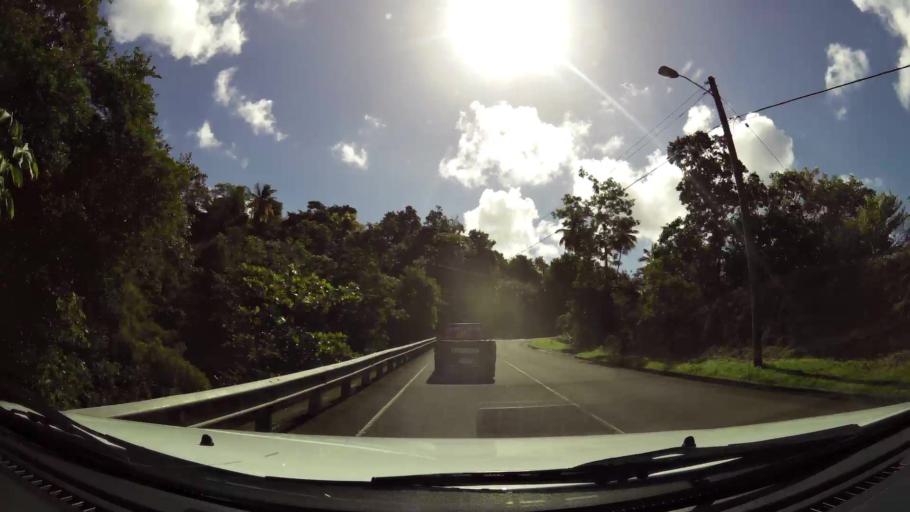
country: LC
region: Choiseul Quarter
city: Choiseul
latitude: 13.7657
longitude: -61.0339
